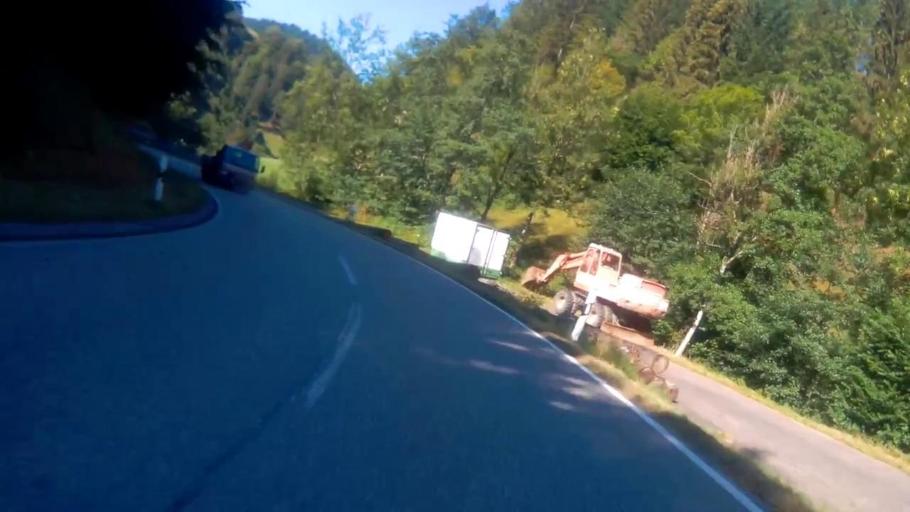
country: DE
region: Baden-Wuerttemberg
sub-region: Freiburg Region
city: Wembach
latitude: 47.7313
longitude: 7.9156
